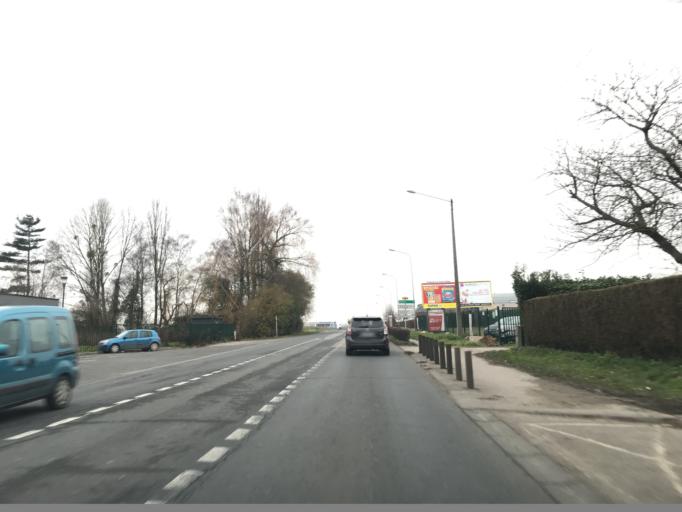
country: FR
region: Haute-Normandie
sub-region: Departement de la Seine-Maritime
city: Boos
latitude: 49.3901
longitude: 1.1982
